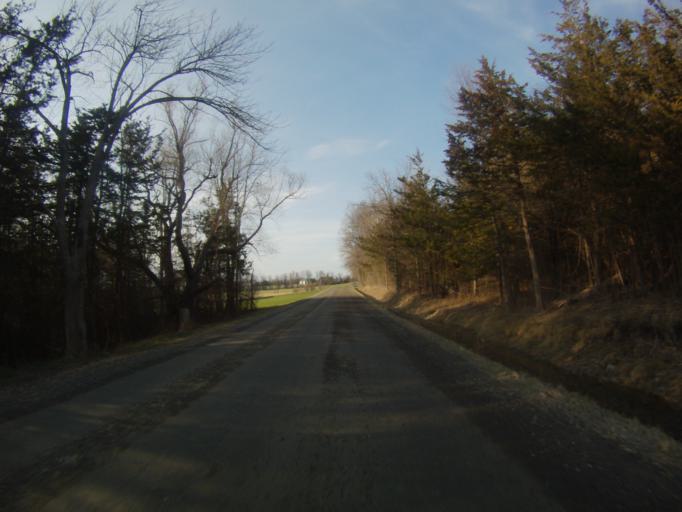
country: US
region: Vermont
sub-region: Addison County
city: Vergennes
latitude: 44.0627
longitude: -73.2932
